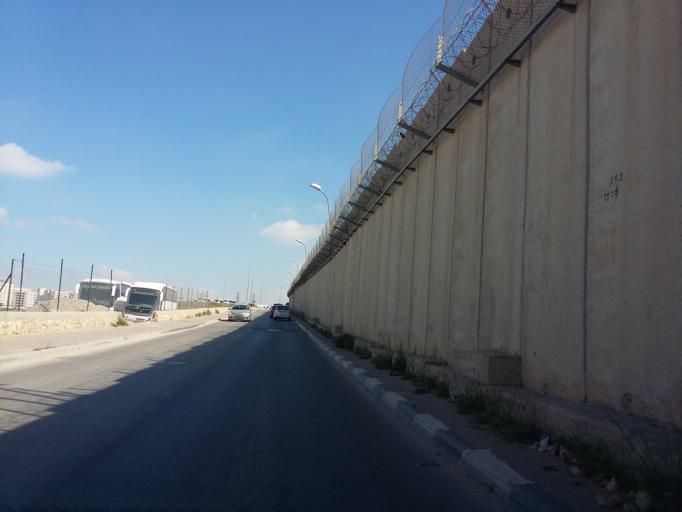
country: PS
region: West Bank
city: Ar Ram wa Dahiyat al Barid
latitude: 31.8576
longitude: 35.2251
